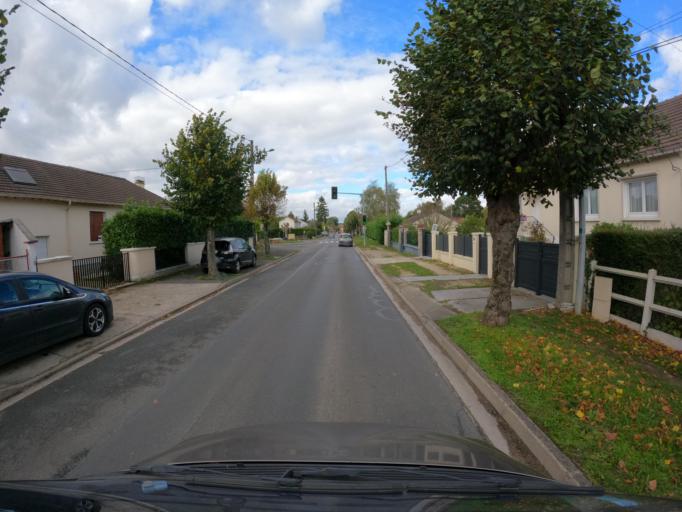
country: FR
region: Ile-de-France
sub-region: Departement de Seine-et-Marne
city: Montry
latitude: 48.8881
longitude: 2.8305
